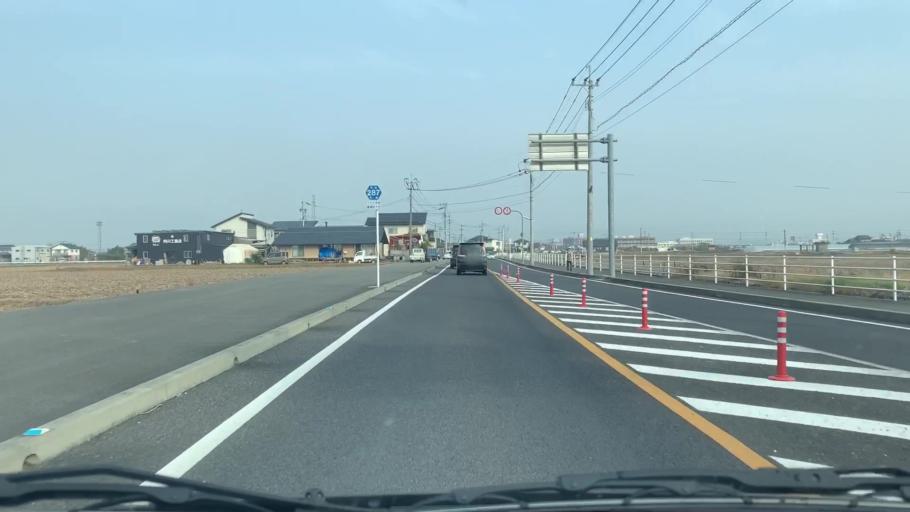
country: JP
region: Saga Prefecture
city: Saga-shi
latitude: 33.2327
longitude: 130.2575
